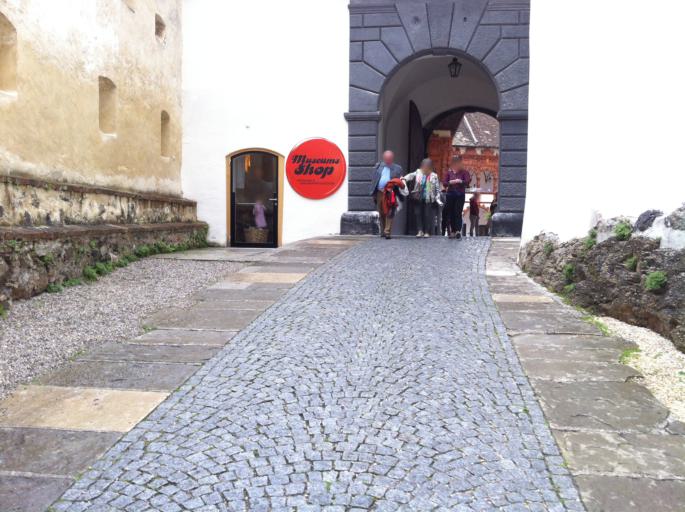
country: AT
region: Lower Austria
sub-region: Politischer Bezirk Melk
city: Melk
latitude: 48.1887
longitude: 15.3558
